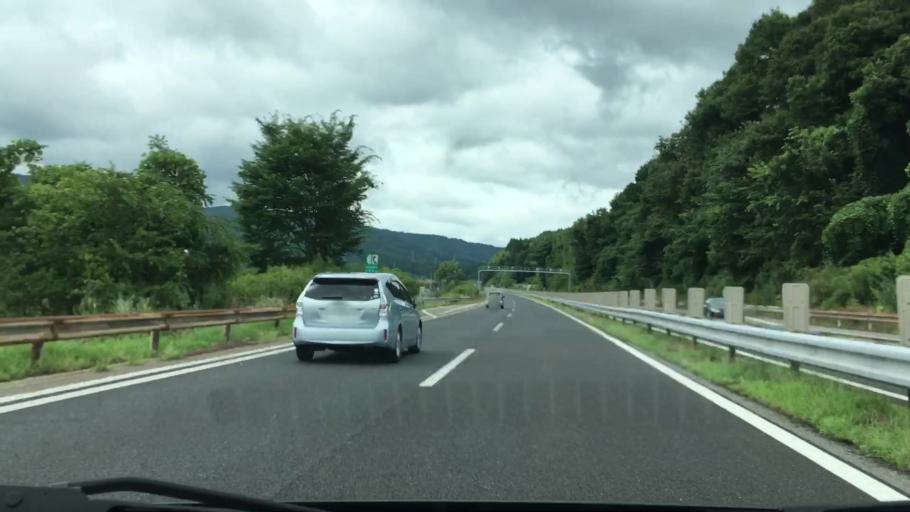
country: JP
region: Okayama
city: Tsuyama
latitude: 35.0633
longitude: 133.8793
